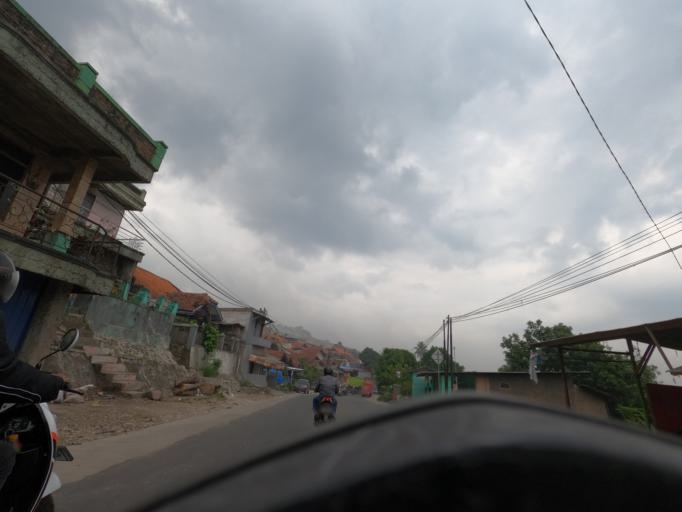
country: ID
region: West Java
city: Padalarang
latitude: -6.8325
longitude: 107.4364
